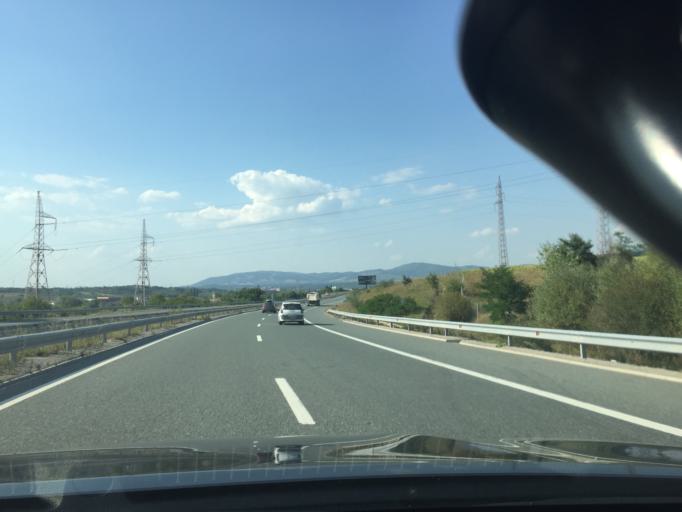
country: BG
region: Pernik
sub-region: Obshtina Pernik
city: Pernik
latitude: 42.5610
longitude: 23.1162
